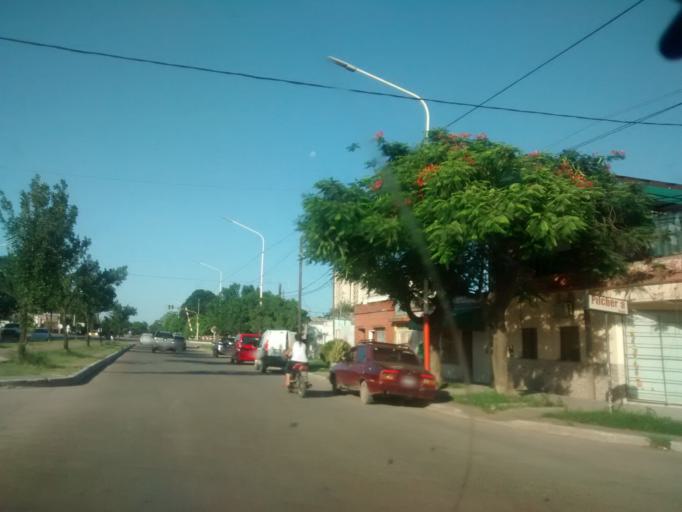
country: AR
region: Chaco
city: Resistencia
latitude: -27.4431
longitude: -59.0061
